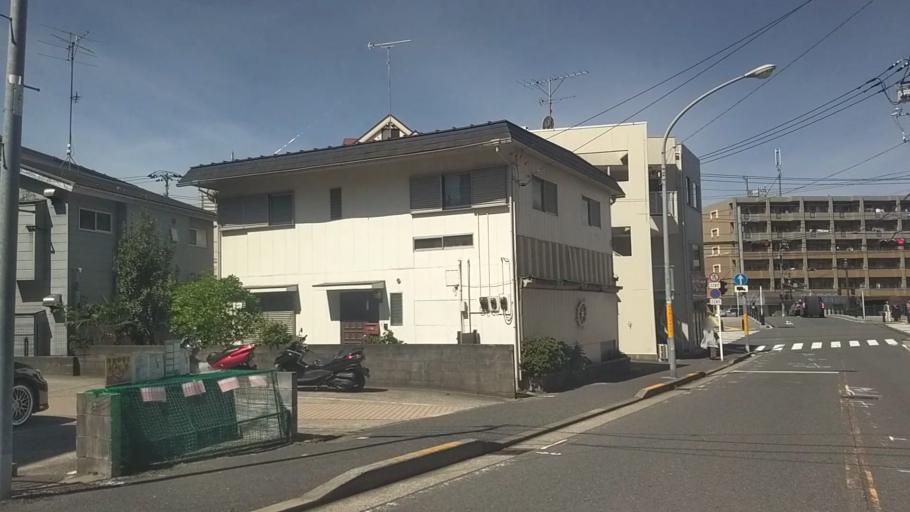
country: JP
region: Kanagawa
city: Yokohama
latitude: 35.4223
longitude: 139.6257
